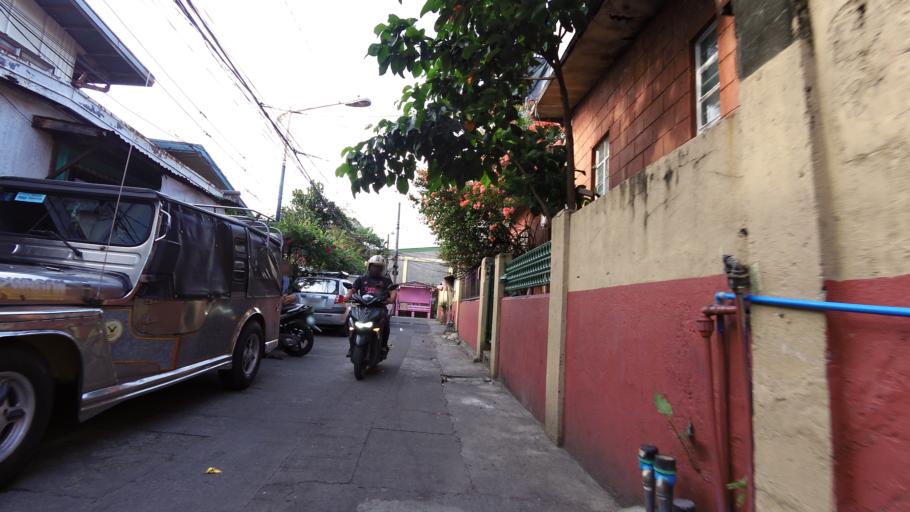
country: PH
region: Metro Manila
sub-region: Pasig
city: Pasig City
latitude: 14.5684
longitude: 121.0780
